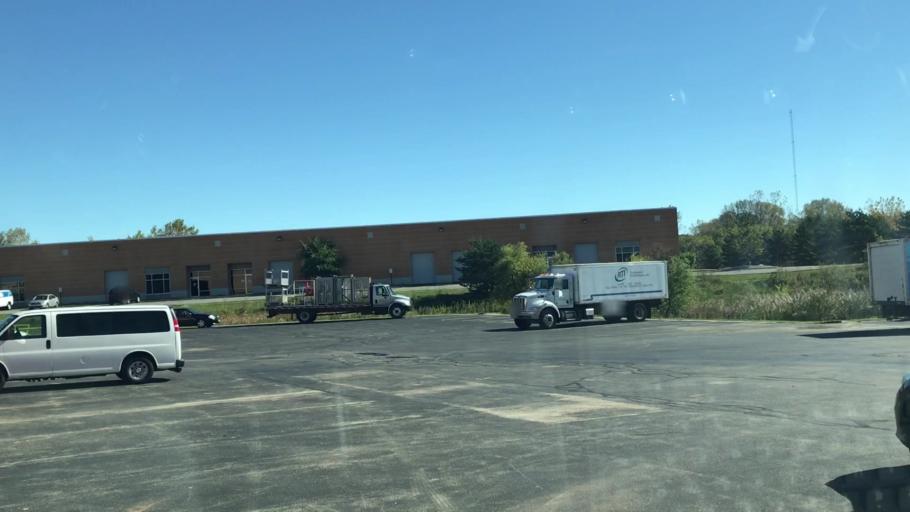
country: US
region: Wisconsin
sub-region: Waukesha County
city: Waukesha
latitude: 43.0186
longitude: -88.1984
